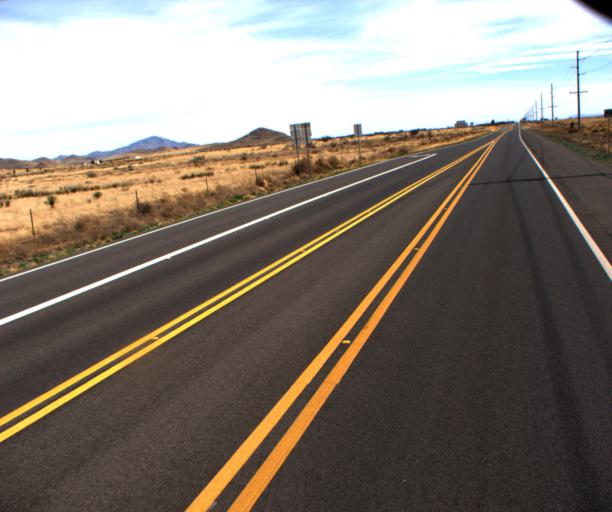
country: US
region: Arizona
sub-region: Cochise County
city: Willcox
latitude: 31.8833
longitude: -109.6952
